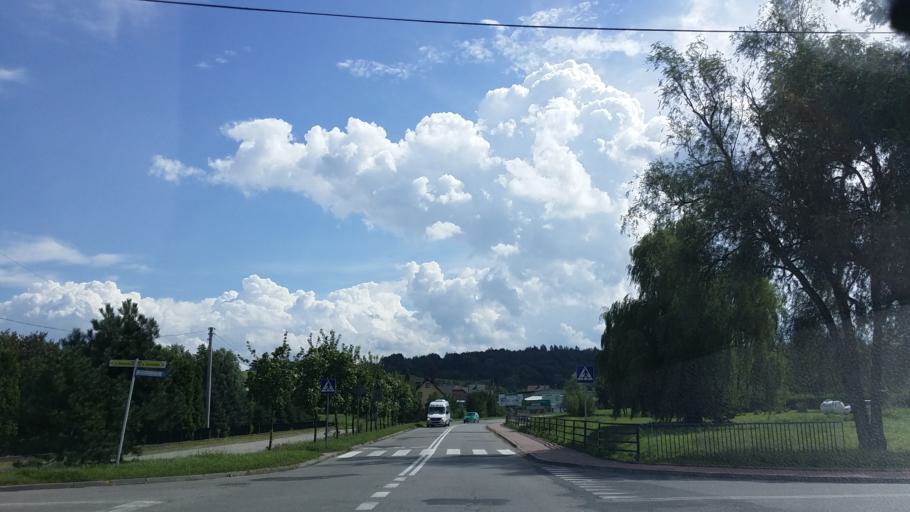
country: PL
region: Lesser Poland Voivodeship
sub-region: Powiat myslenicki
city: Dobczyce
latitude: 49.8801
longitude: 20.1038
